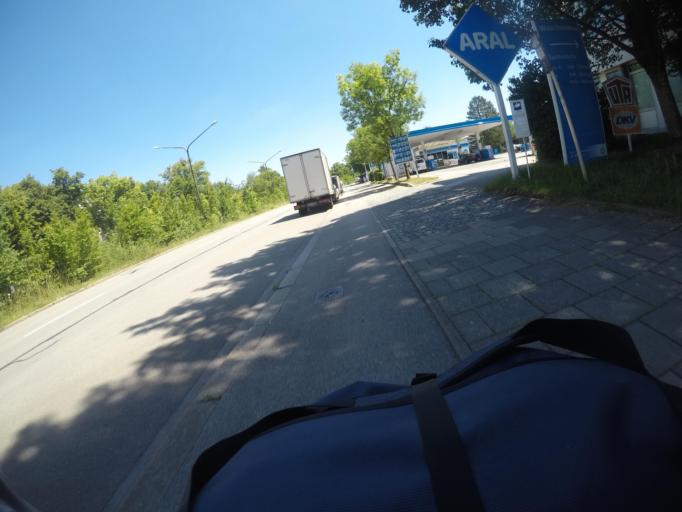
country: DE
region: Bavaria
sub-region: Upper Bavaria
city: Pullach im Isartal
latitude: 48.0985
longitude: 11.5178
